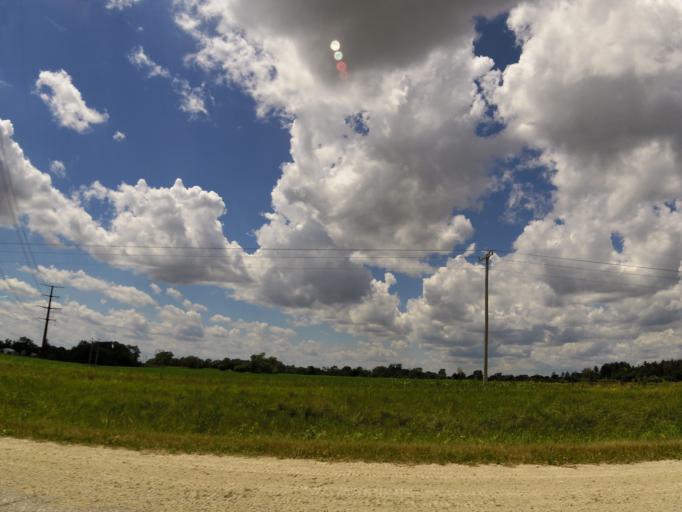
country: US
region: Iowa
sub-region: Fayette County
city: Oelwein
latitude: 42.5865
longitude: -91.9046
